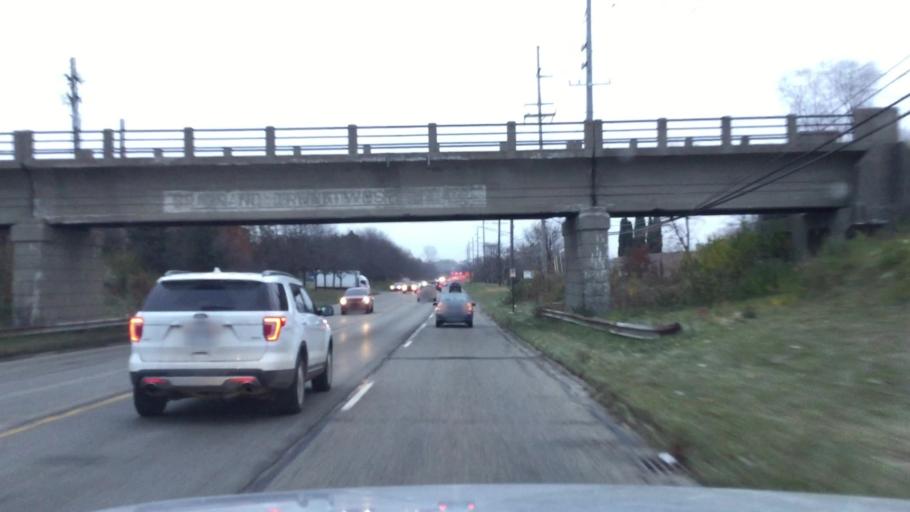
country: US
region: Michigan
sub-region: Oakland County
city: Pontiac
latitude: 42.6350
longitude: -83.2591
